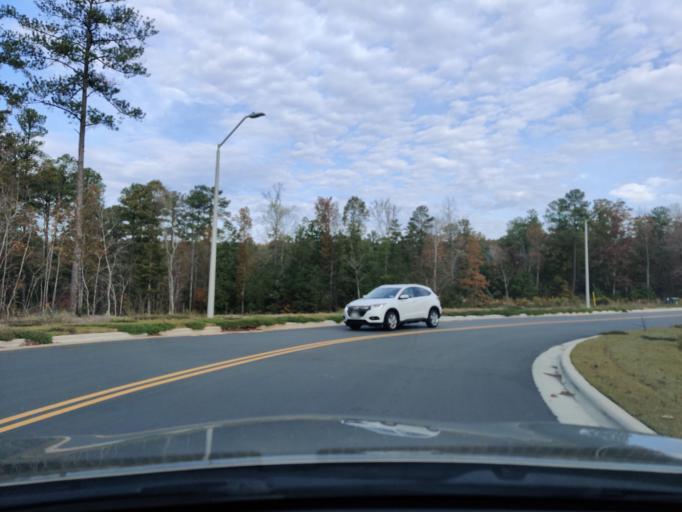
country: US
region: North Carolina
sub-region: Wake County
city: Morrisville
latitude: 35.8442
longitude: -78.8628
